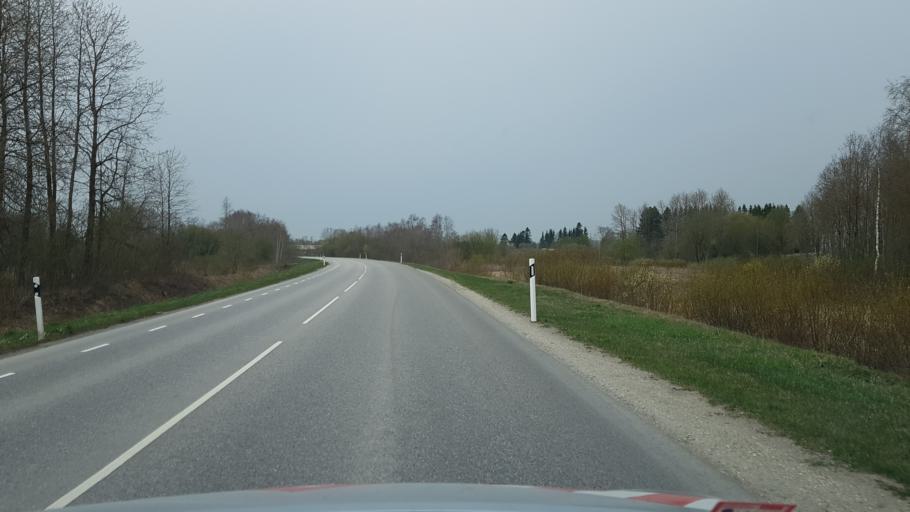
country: EE
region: Harju
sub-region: Joelaehtme vald
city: Loo
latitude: 59.4107
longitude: 24.9284
